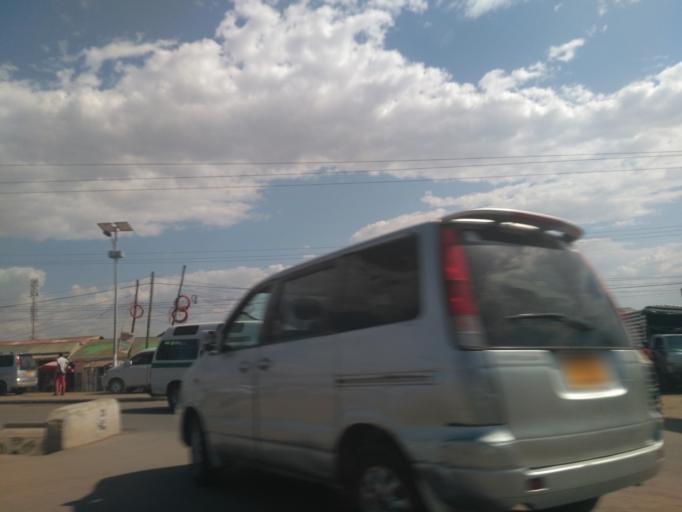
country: TZ
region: Mwanza
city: Mwanza
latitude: -2.5398
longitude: 32.9541
